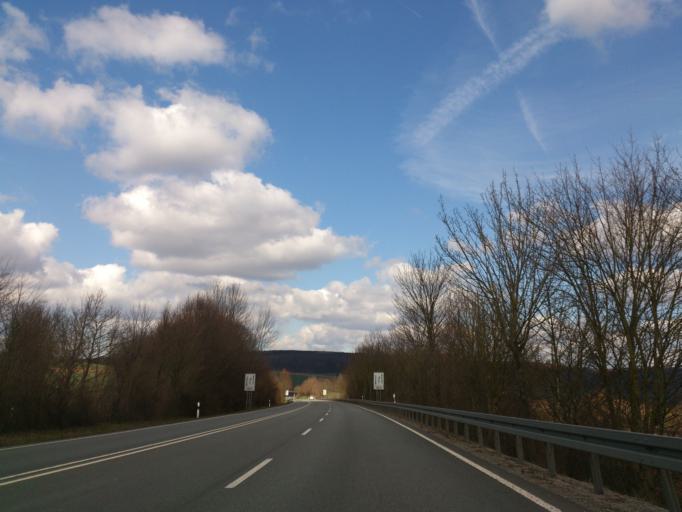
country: DE
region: North Rhine-Westphalia
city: Brakel
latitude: 51.7038
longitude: 9.2282
